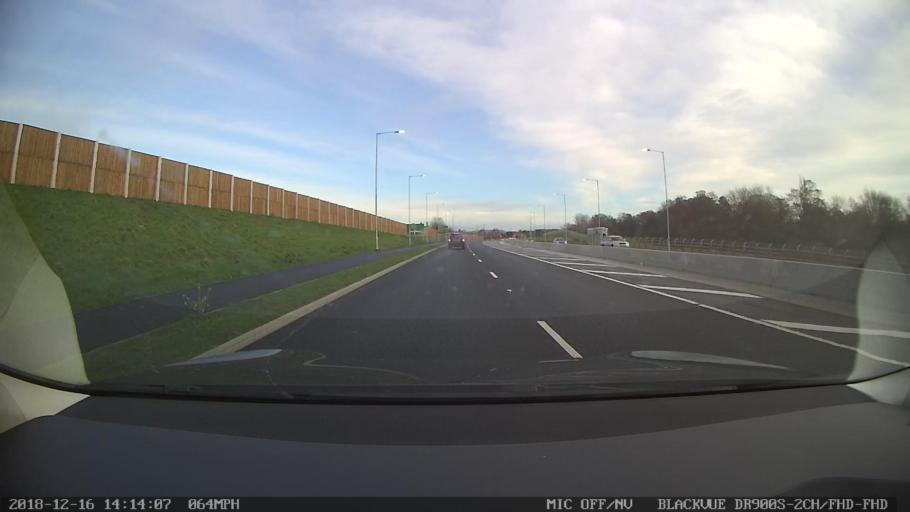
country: GB
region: England
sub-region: Cheshire East
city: Poynton
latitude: 53.3648
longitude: -2.1189
